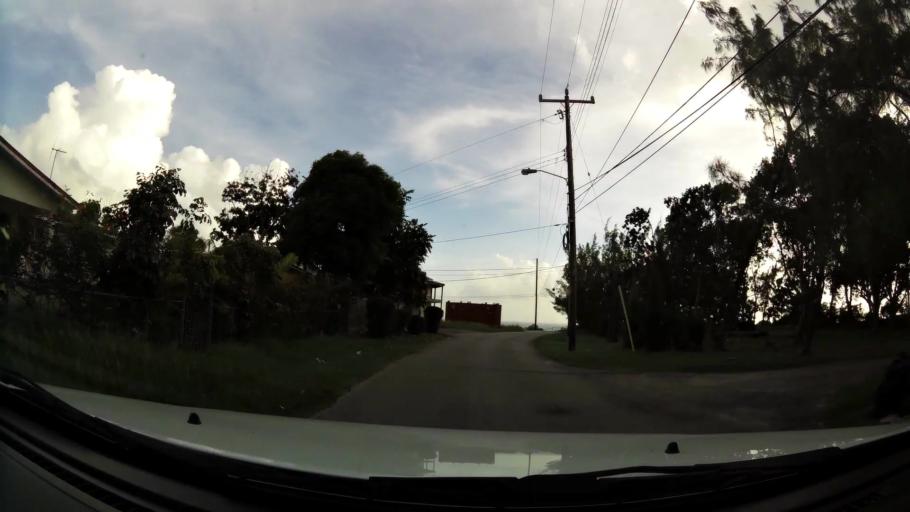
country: BB
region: Christ Church
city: Oistins
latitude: 13.0684
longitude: -59.5336
